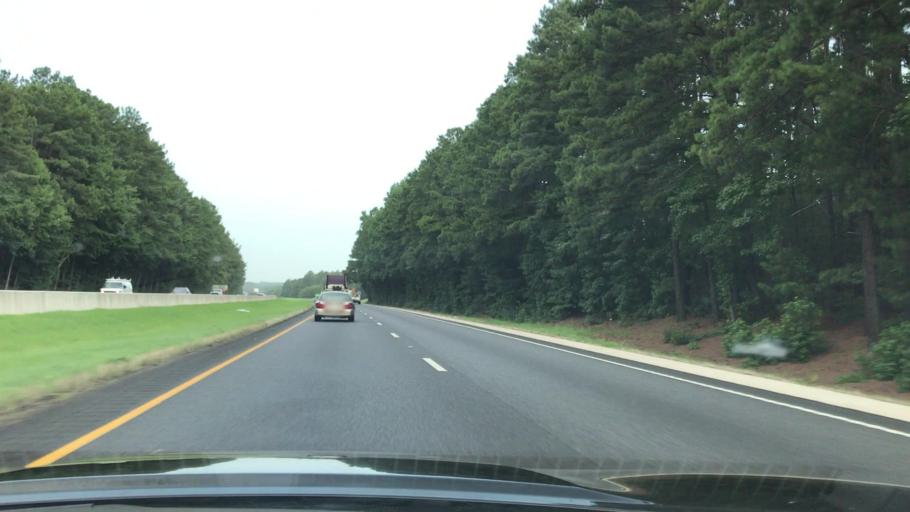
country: US
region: Texas
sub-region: Gregg County
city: Longview
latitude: 32.4352
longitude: -94.7977
